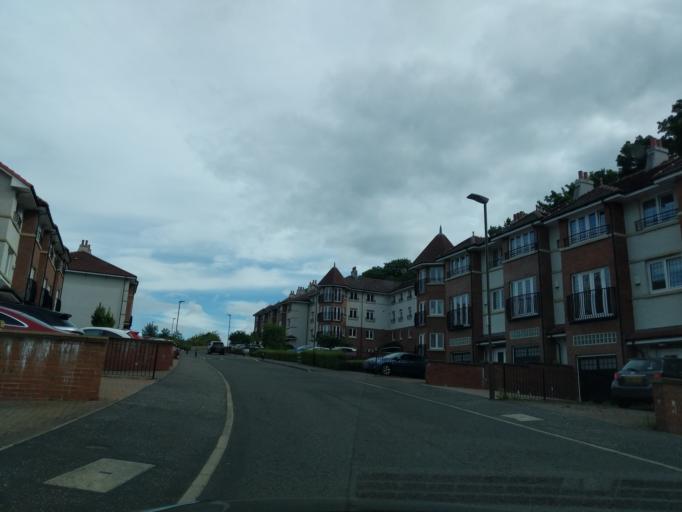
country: GB
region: Scotland
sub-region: Edinburgh
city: Colinton
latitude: 55.9583
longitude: -3.2720
